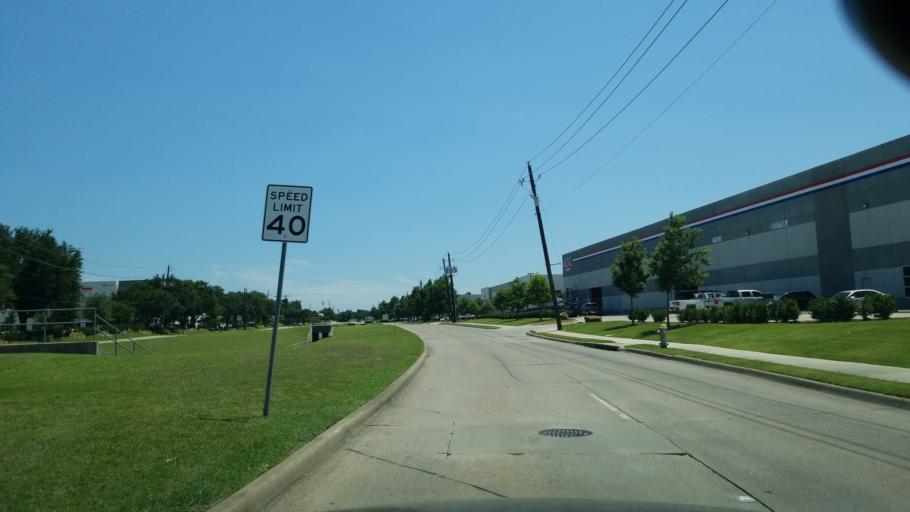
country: US
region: Texas
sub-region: Dallas County
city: Carrollton
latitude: 32.9460
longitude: -96.9168
